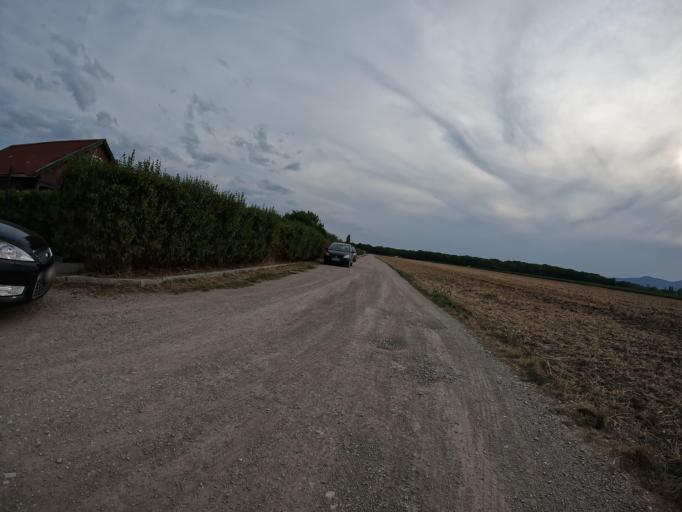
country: AT
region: Lower Austria
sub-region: Politischer Bezirk Baden
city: Trumau
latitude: 47.9992
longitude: 16.3358
